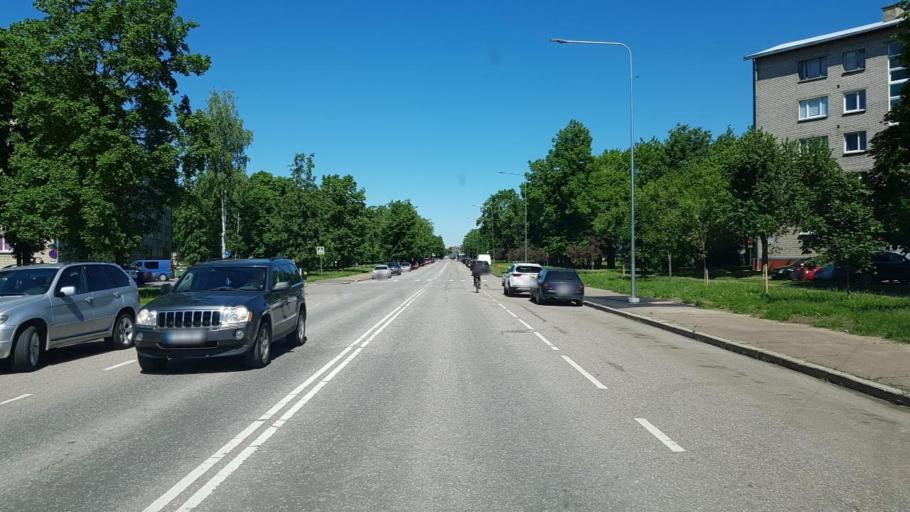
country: EE
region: Ida-Virumaa
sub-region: Narva linn
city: Narva
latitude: 59.3752
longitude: 28.1749
